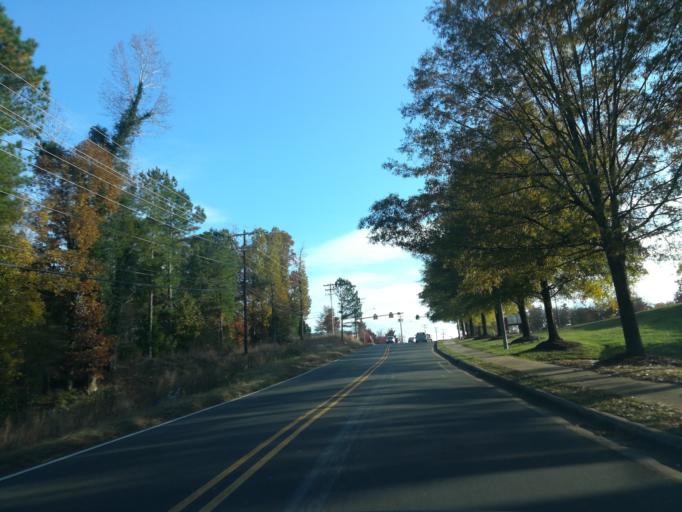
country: US
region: North Carolina
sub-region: Orange County
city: Chapel Hill
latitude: 35.9568
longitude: -78.9948
